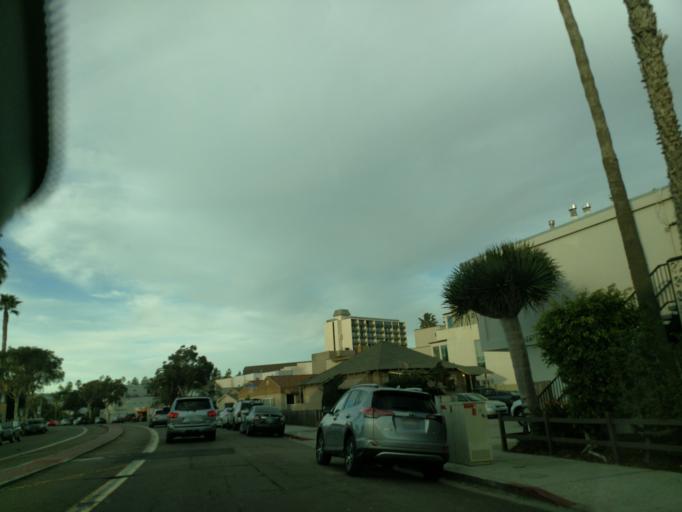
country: US
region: California
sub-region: San Diego County
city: La Jolla
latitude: 32.7883
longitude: -117.2533
